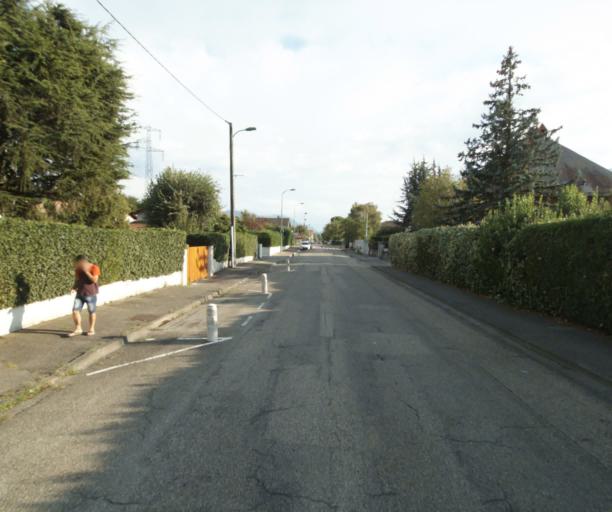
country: FR
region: Rhone-Alpes
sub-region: Departement de l'Isere
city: Seyssinet-Pariset
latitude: 45.1731
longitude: 5.6992
